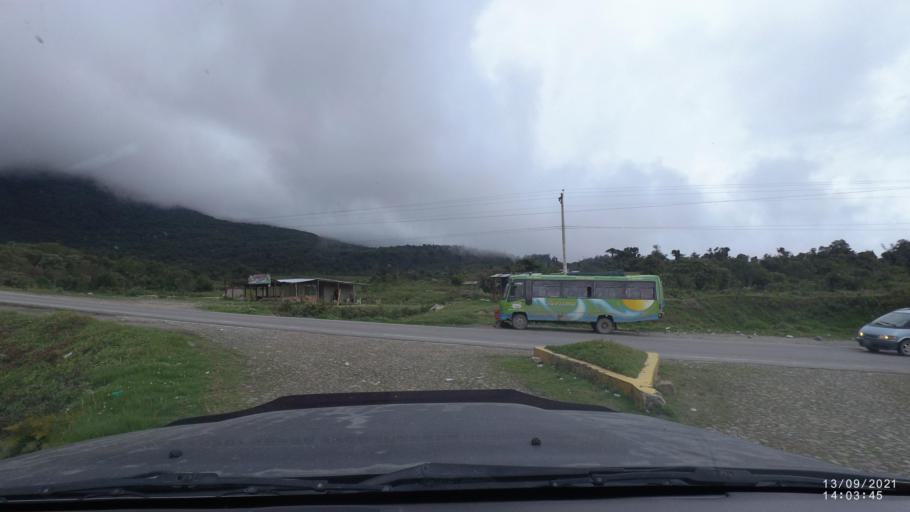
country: BO
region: Cochabamba
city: Colomi
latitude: -17.2037
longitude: -65.8676
